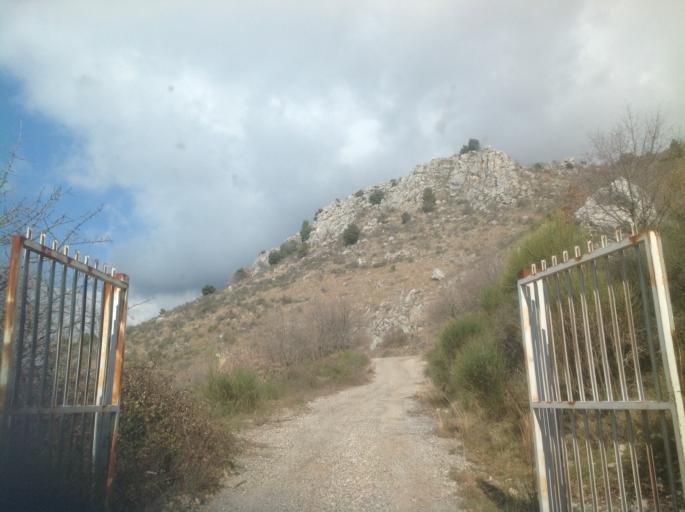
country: IT
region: Calabria
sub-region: Provincia di Cosenza
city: Frascineto
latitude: 39.8455
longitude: 16.2603
